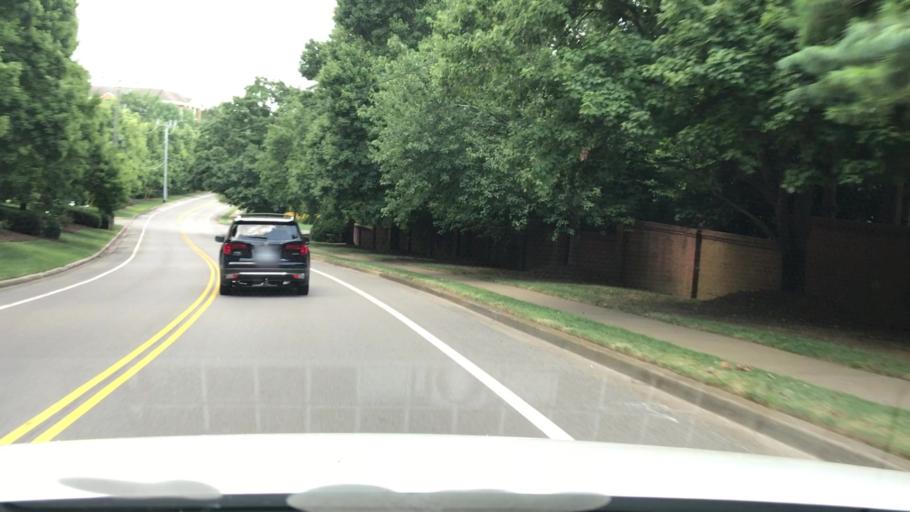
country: US
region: Tennessee
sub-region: Davidson County
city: Belle Meade
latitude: 36.1303
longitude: -86.8213
